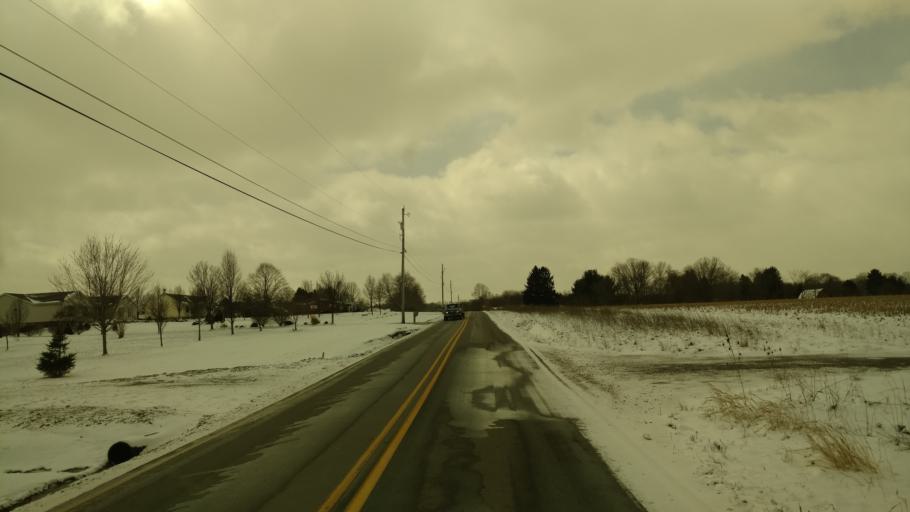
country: US
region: Pennsylvania
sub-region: Mercer County
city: Greenville
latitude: 41.3956
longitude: -80.3498
